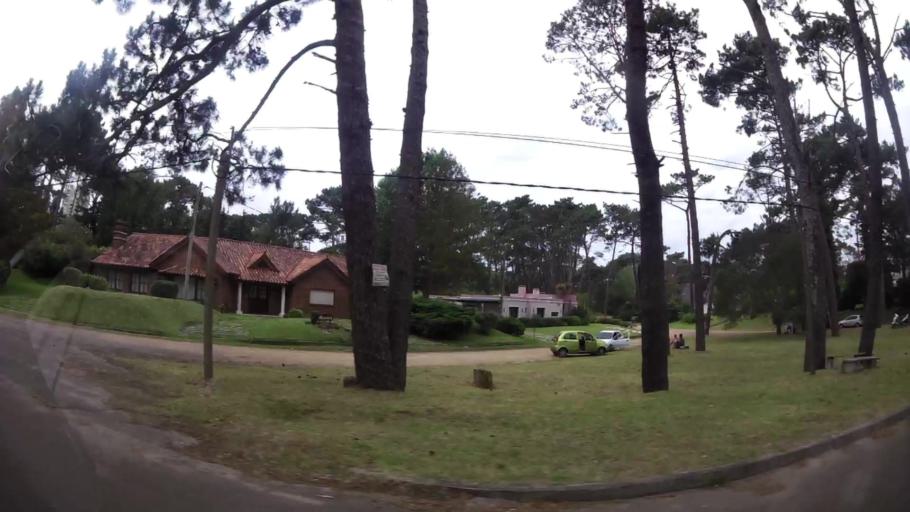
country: UY
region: Maldonado
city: Maldonado
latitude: -34.9264
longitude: -54.9530
